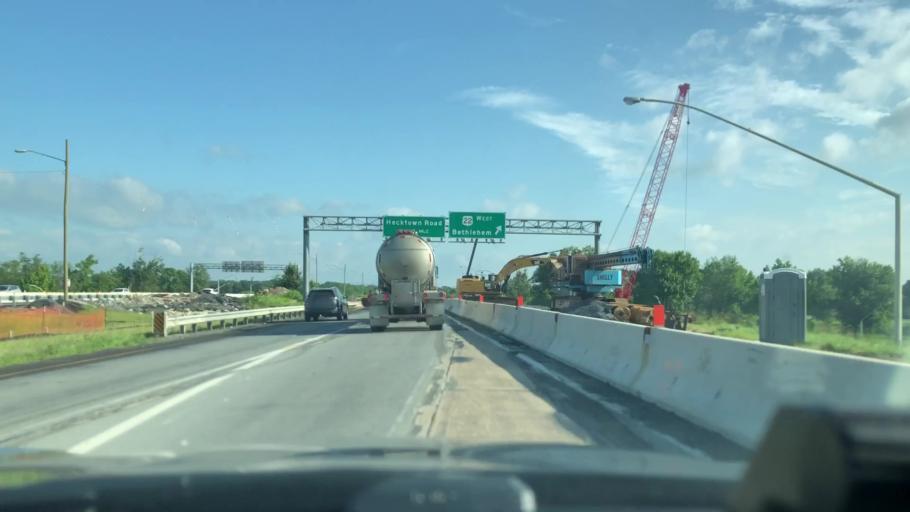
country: US
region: Pennsylvania
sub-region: Northampton County
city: Palmer Heights
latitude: 40.6821
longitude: -75.2884
